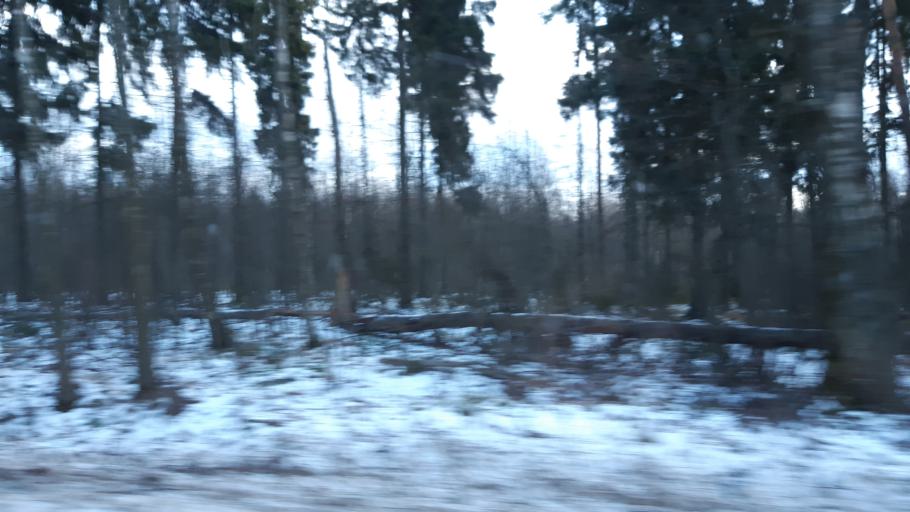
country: RU
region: Moskovskaya
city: Noginsk-9
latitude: 55.9728
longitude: 38.5383
